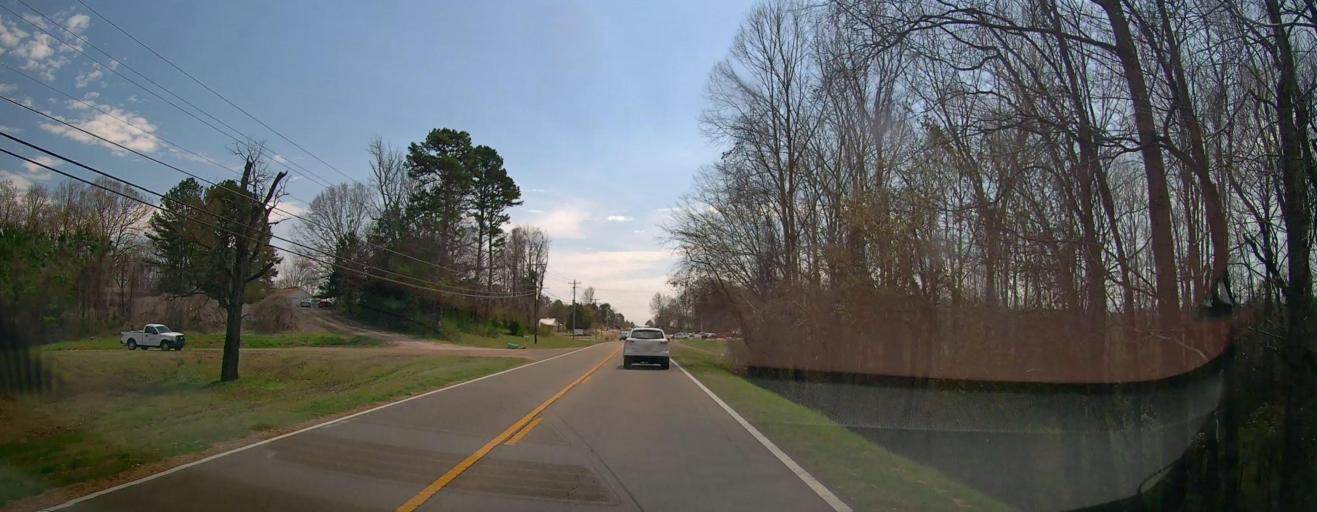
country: US
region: Mississippi
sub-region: Union County
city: New Albany
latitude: 34.4603
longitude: -88.9786
